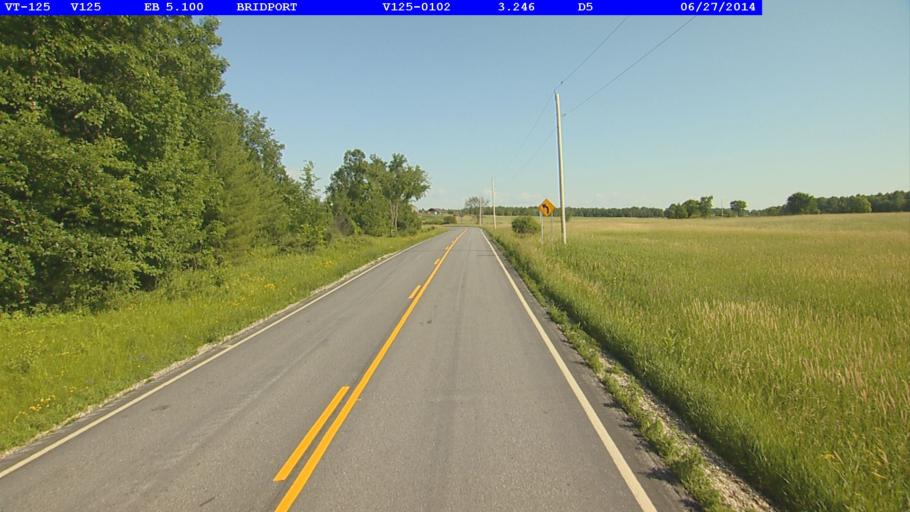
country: US
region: New York
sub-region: Essex County
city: Port Henry
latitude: 43.9933
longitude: -73.3492
